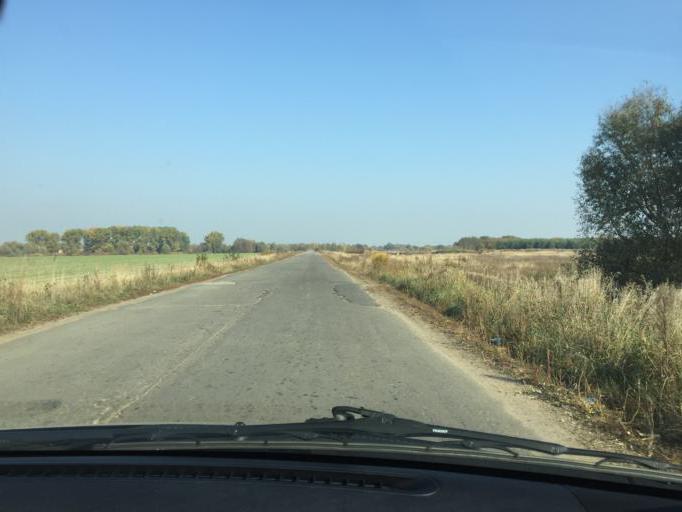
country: BY
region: Brest
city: Davyd-Haradok
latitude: 52.0720
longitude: 27.2420
